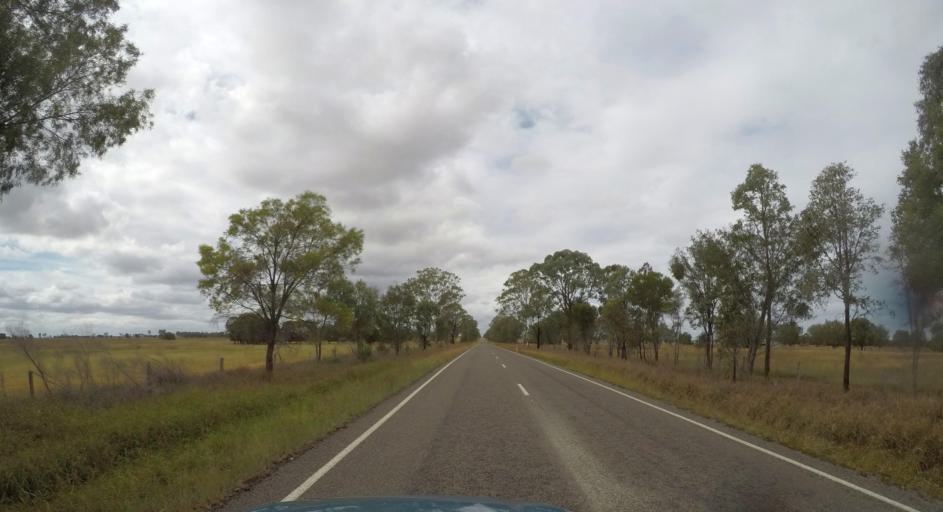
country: AU
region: Queensland
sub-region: South Burnett
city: Kingaroy
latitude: -26.3922
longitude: 151.2192
